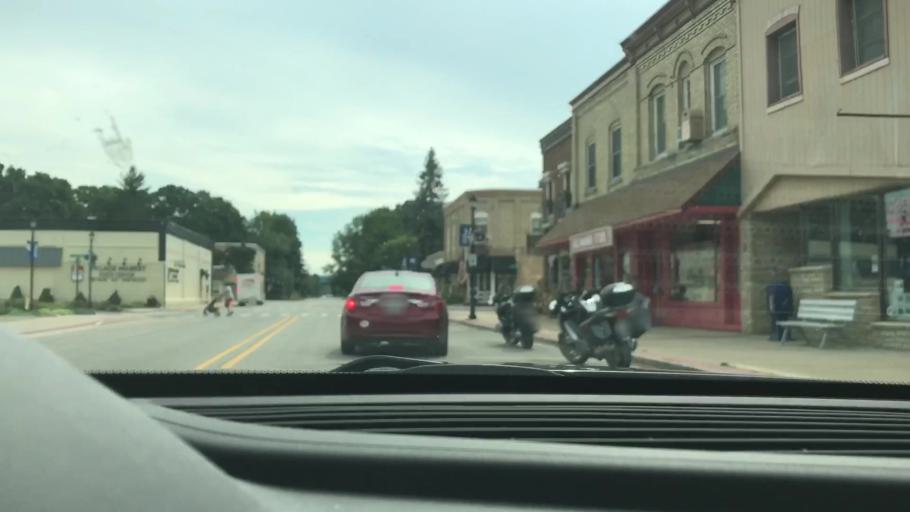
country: US
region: Michigan
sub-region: Antrim County
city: Bellaire
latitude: 45.0706
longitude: -85.2642
